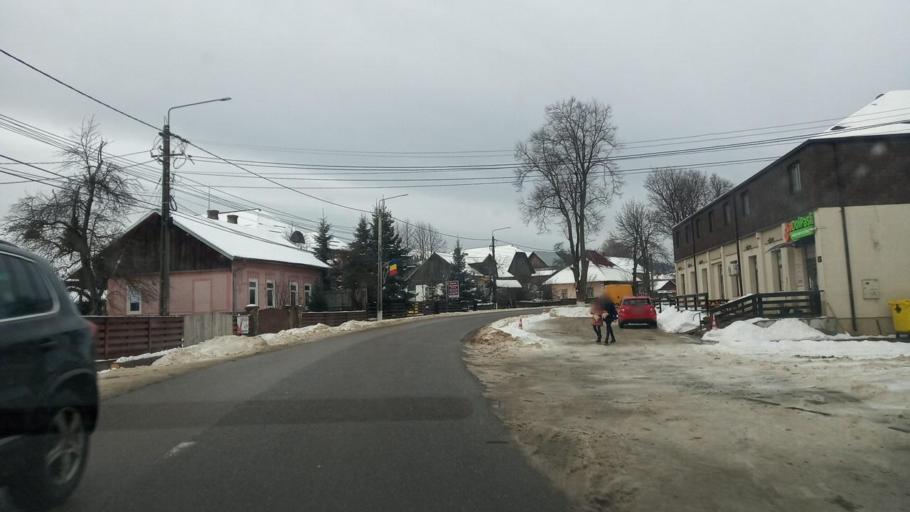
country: RO
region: Suceava
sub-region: Comuna Manastirea Humorului
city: Manastirea Humorului
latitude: 47.5918
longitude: 25.8625
